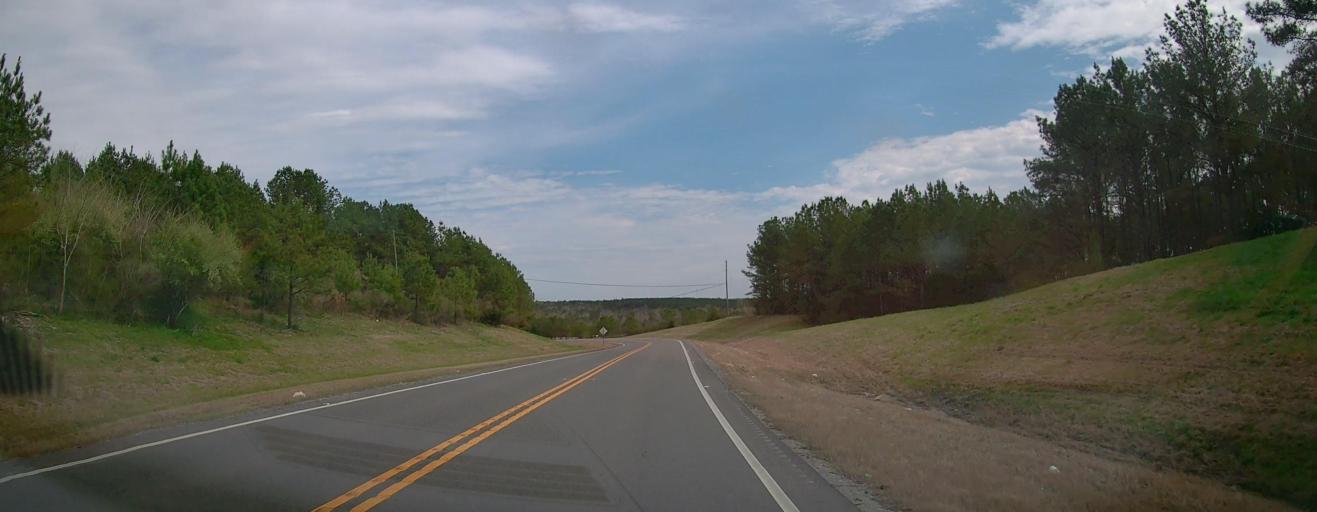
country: US
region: Alabama
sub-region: Walker County
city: Carbon Hill
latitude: 33.8662
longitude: -87.4104
